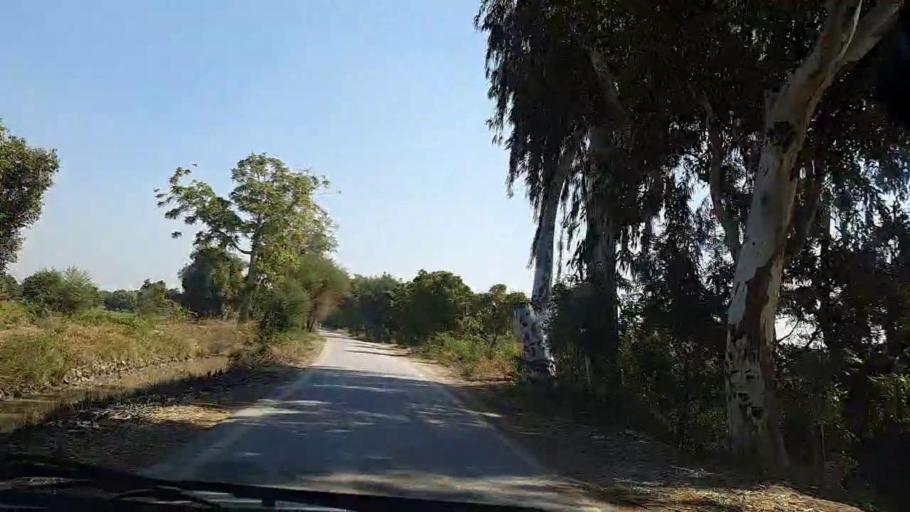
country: PK
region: Sindh
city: Mirpur Khas
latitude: 25.4712
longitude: 69.0183
